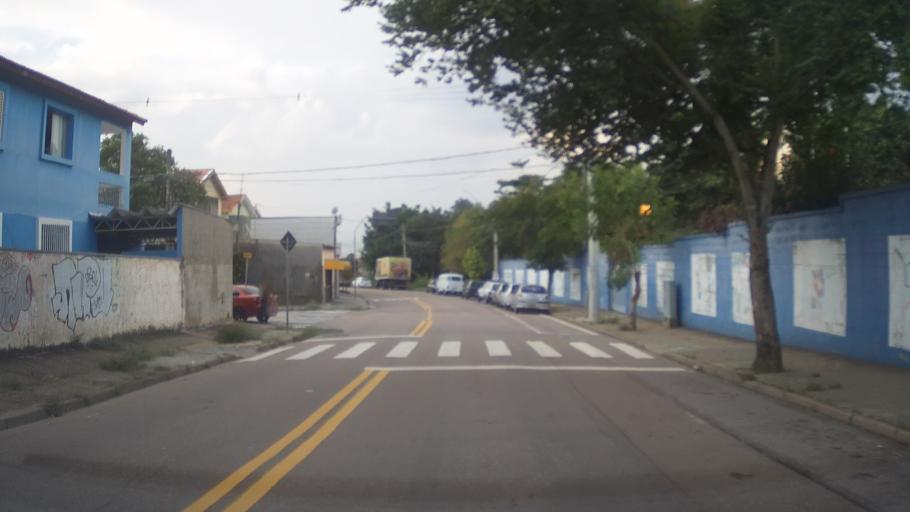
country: BR
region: Sao Paulo
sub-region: Jundiai
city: Jundiai
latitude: -23.1842
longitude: -46.9628
